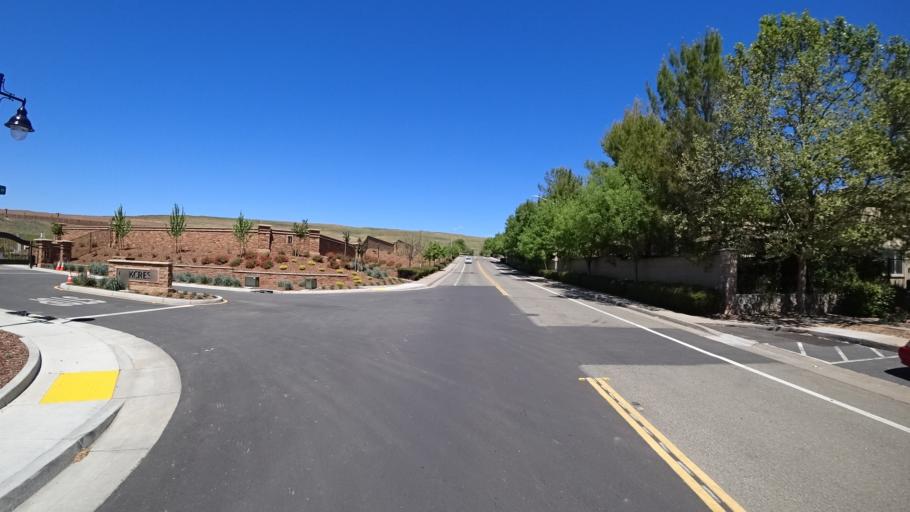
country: US
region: California
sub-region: Placer County
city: Rocklin
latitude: 38.8375
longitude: -121.2472
